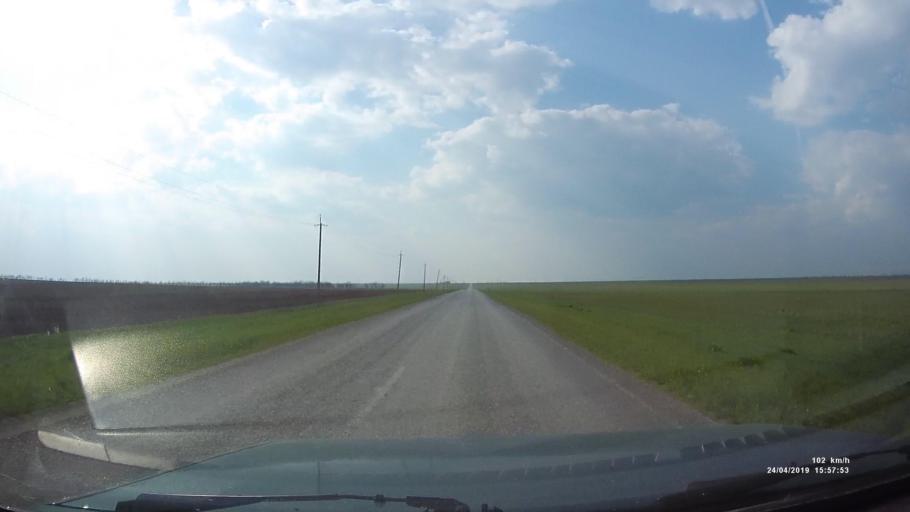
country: RU
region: Kalmykiya
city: Yashalta
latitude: 46.6091
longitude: 42.5003
